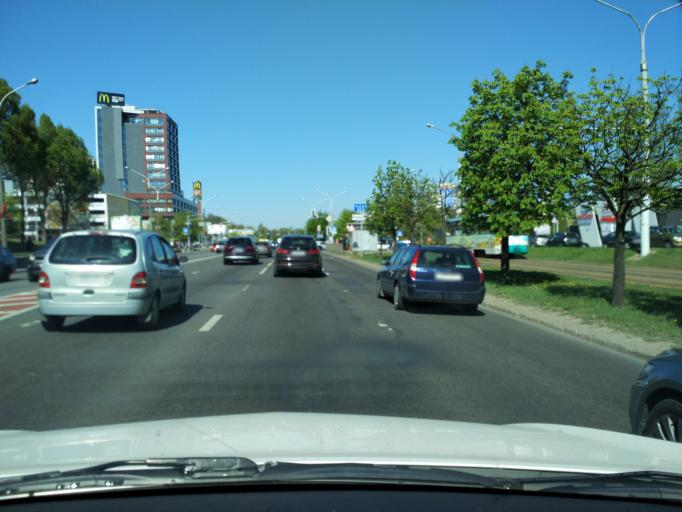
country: BY
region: Minsk
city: Bal'shavik
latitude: 53.9533
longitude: 27.6192
